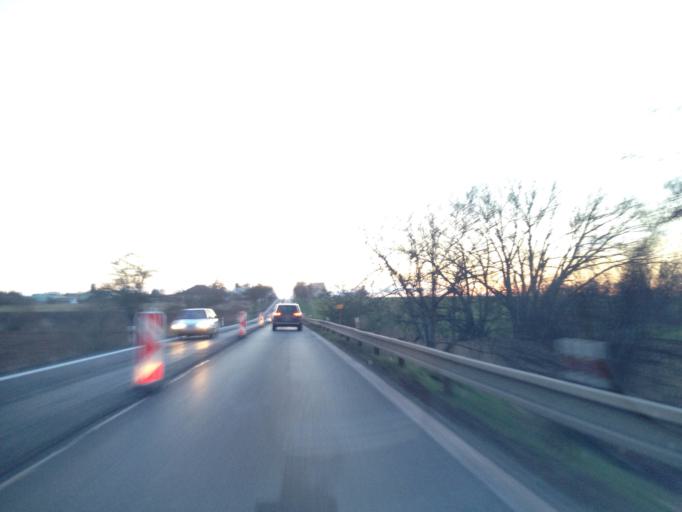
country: CZ
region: Central Bohemia
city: Jesenice
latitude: 50.1570
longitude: 13.5413
